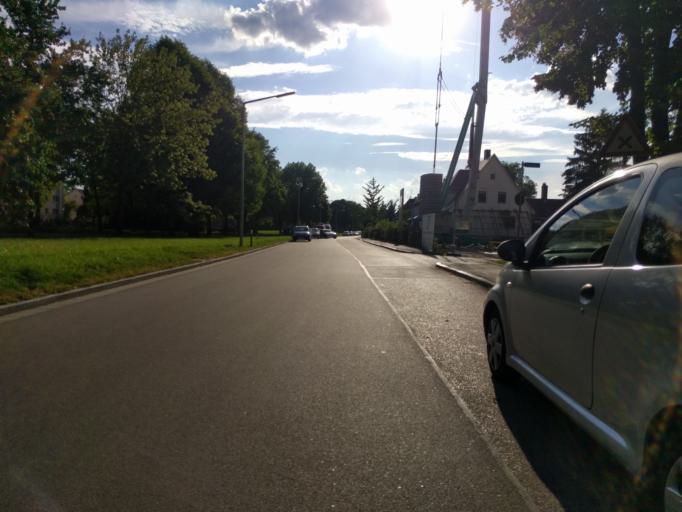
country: DE
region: Bavaria
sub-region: Upper Palatinate
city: Regensburg
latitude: 49.0020
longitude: 12.1137
